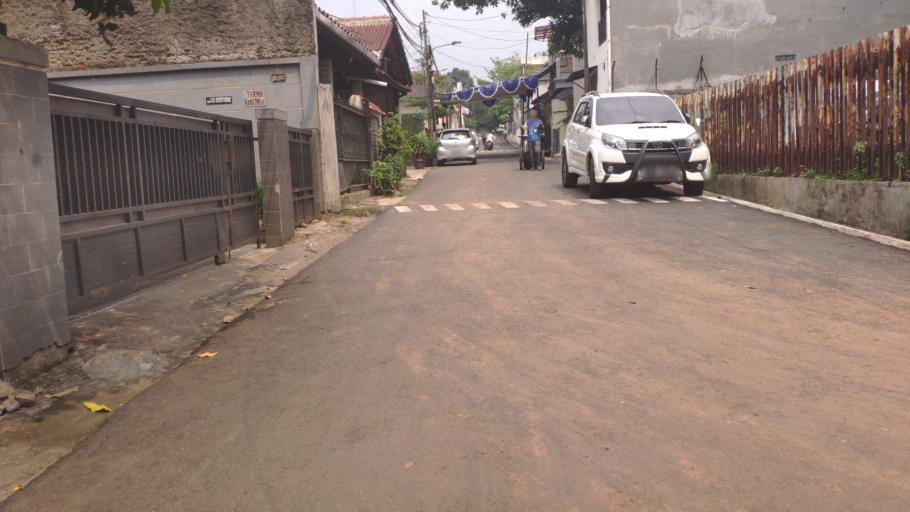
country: ID
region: Jakarta Raya
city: Jakarta
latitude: -6.2638
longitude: 106.8296
